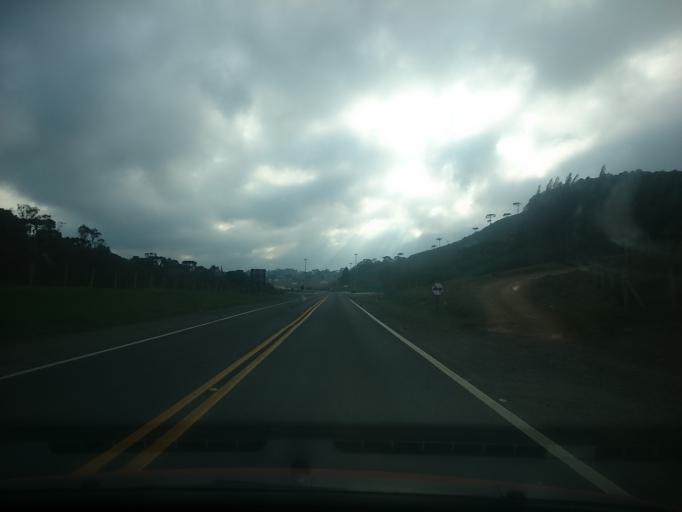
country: BR
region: Santa Catarina
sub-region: Lages
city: Lages
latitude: -27.9576
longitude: -50.4860
